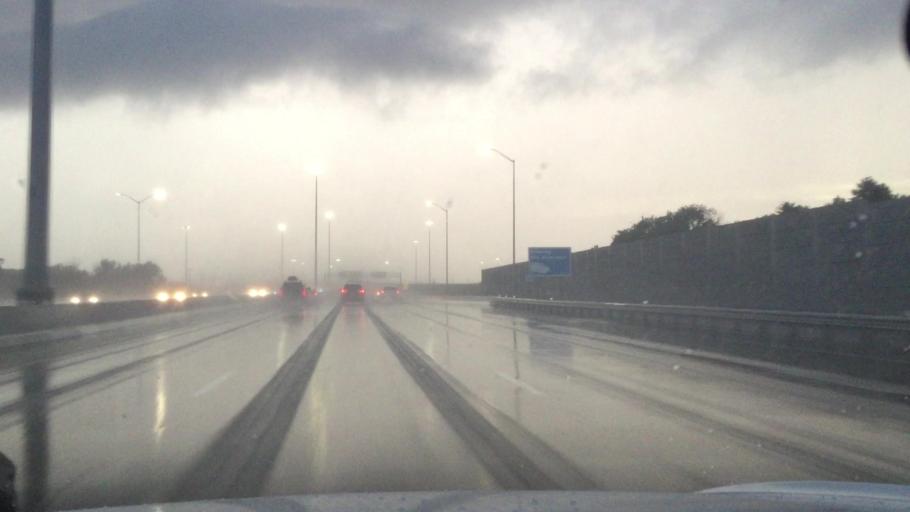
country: CA
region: Ontario
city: Ajax
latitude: 43.8655
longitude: -78.9629
